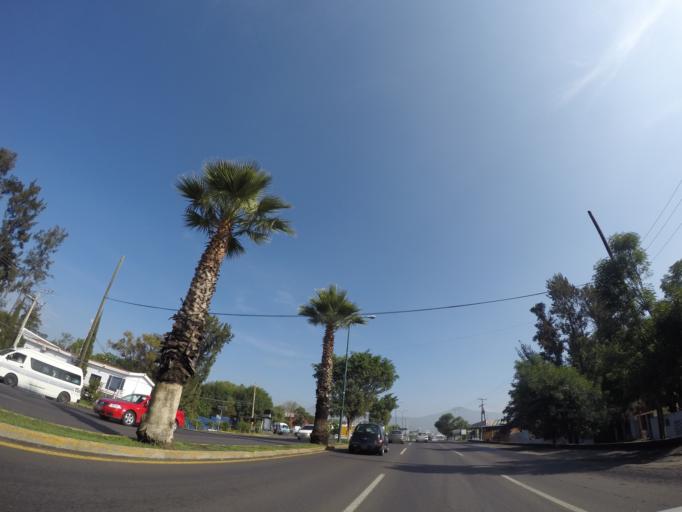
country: MX
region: Michoacan
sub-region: Morelia
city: San Antonio
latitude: 19.6869
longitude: -101.2378
